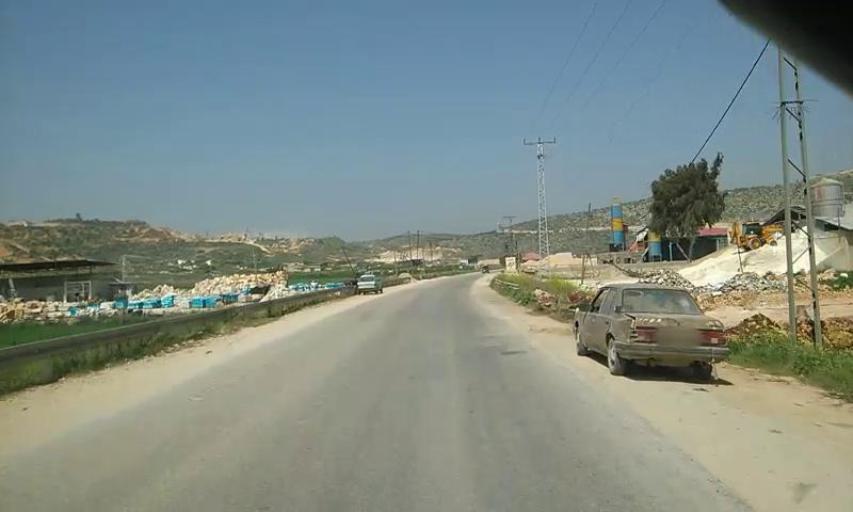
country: PS
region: West Bank
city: Az Zababidah
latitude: 32.3965
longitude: 35.3197
